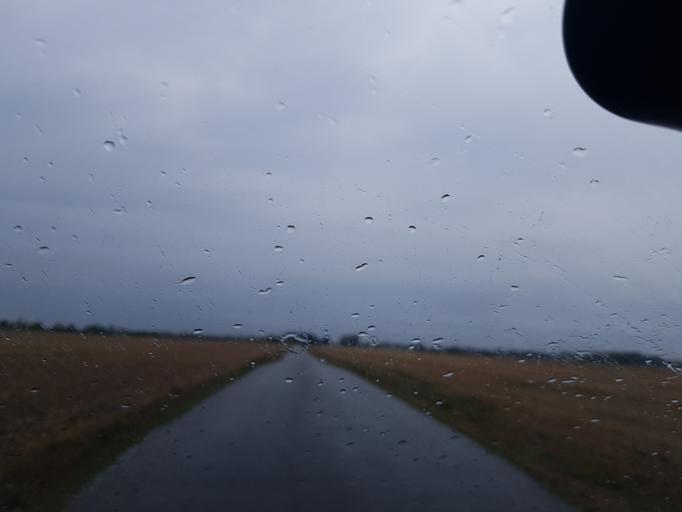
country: DE
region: Saxony-Anhalt
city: Jessen
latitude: 51.7804
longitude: 12.8856
